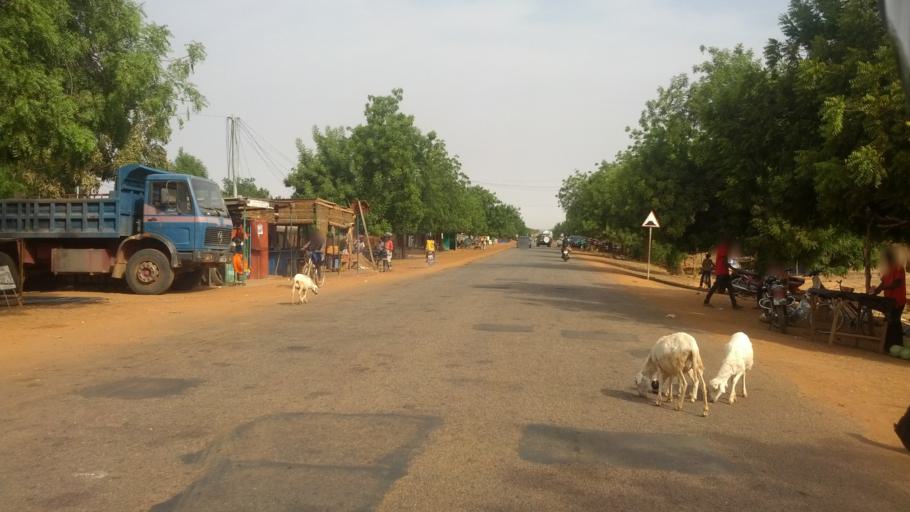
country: BF
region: Centre-Nord
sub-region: Province du Sanmatenga
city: Kaya
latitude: 12.9100
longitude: -1.0782
